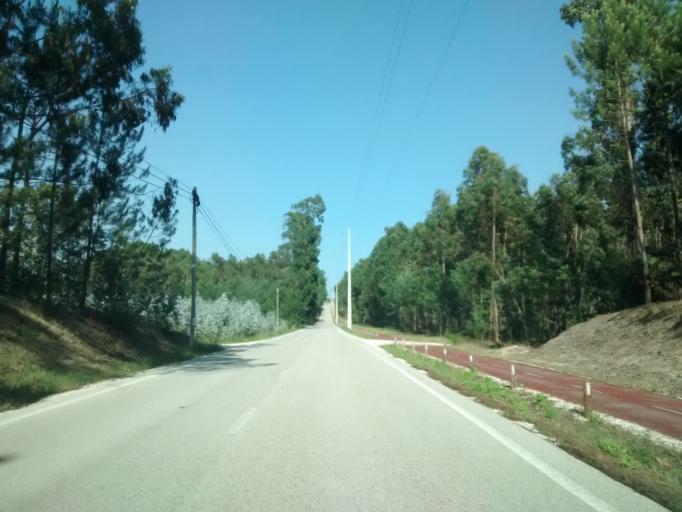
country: PT
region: Leiria
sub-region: Leiria
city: Monte Redondo
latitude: 39.9798
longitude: -8.8229
